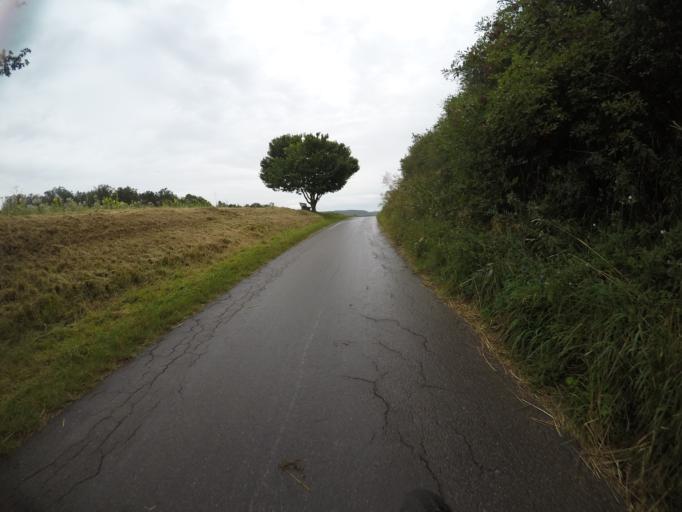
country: DE
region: Baden-Wuerttemberg
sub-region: Regierungsbezirk Stuttgart
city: Ehningen
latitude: 48.6482
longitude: 8.9375
